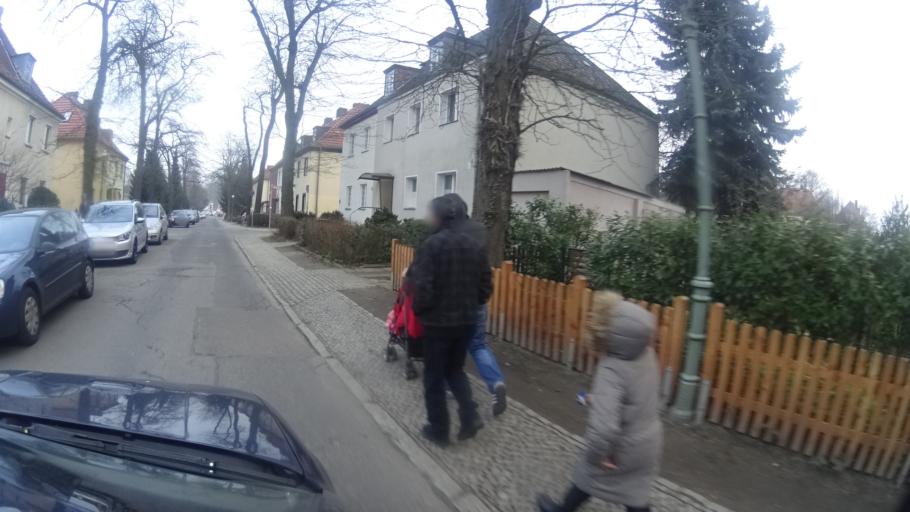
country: DE
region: Berlin
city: Tempelhof Bezirk
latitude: 52.4782
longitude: 13.3794
